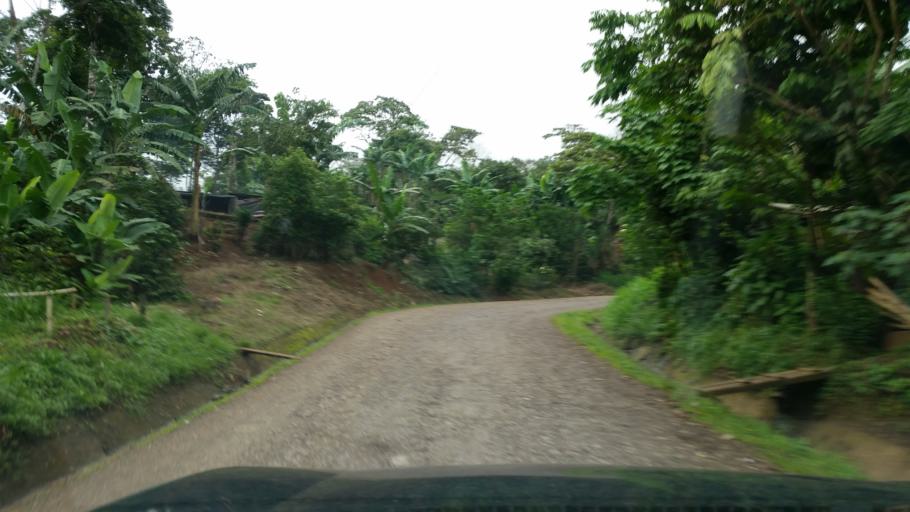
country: NI
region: Jinotega
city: San Jose de Bocay
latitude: 13.2762
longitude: -85.7273
